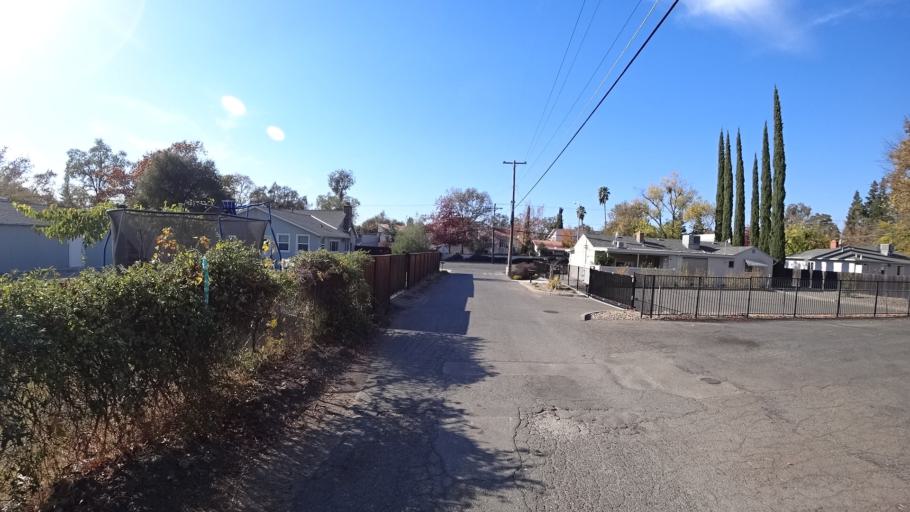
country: US
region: California
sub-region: Sacramento County
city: Fair Oaks
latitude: 38.6707
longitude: -121.2917
